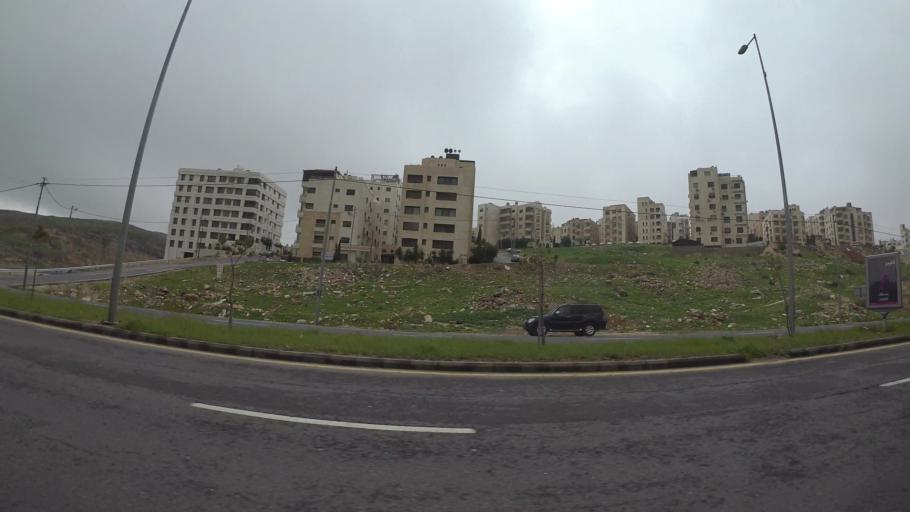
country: JO
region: Amman
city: Al Bunayyat ash Shamaliyah
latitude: 31.9365
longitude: 35.8724
